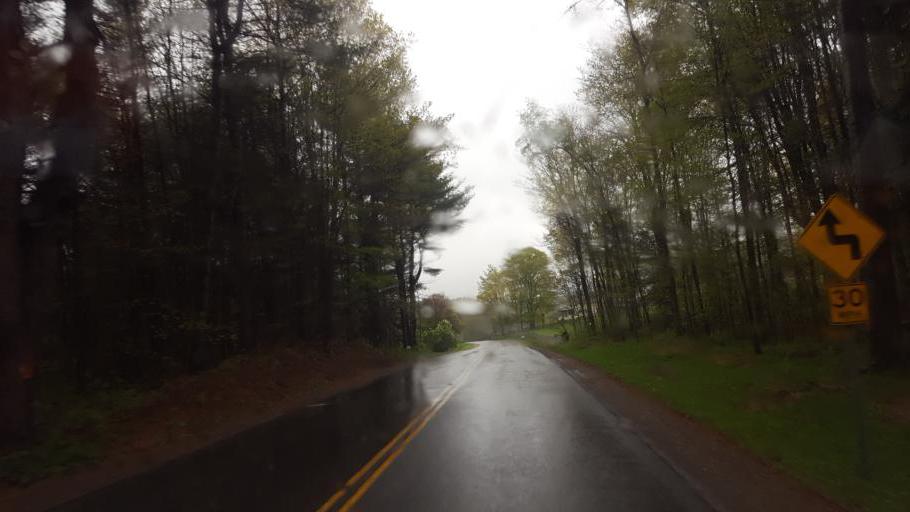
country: US
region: Pennsylvania
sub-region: Tioga County
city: Elkland
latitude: 42.0756
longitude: -77.3983
